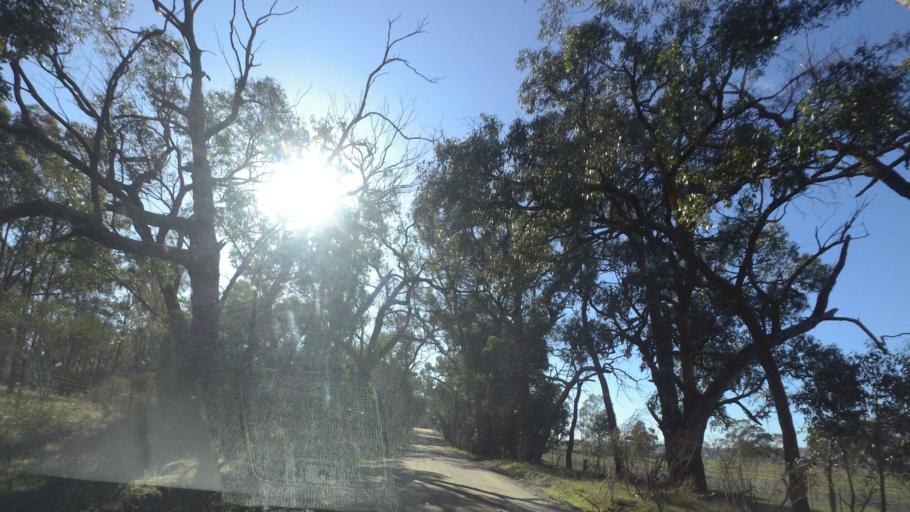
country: AU
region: Victoria
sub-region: Mount Alexander
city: Castlemaine
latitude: -37.1277
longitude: 144.4083
